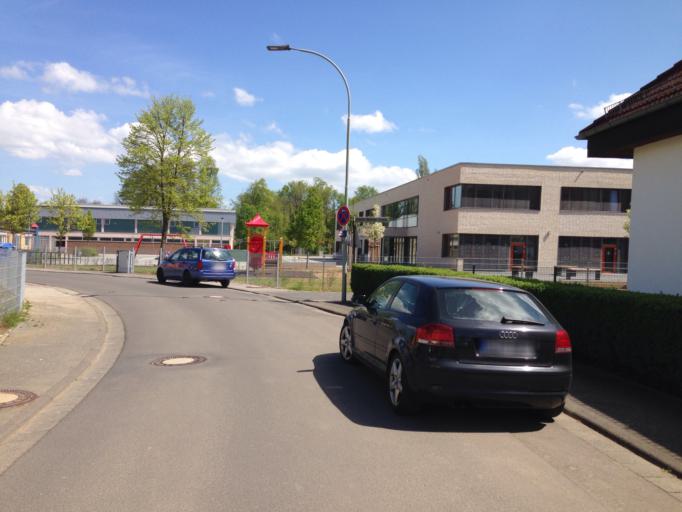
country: DE
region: Hesse
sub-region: Regierungsbezirk Giessen
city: Lich
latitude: 50.5164
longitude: 8.8115
